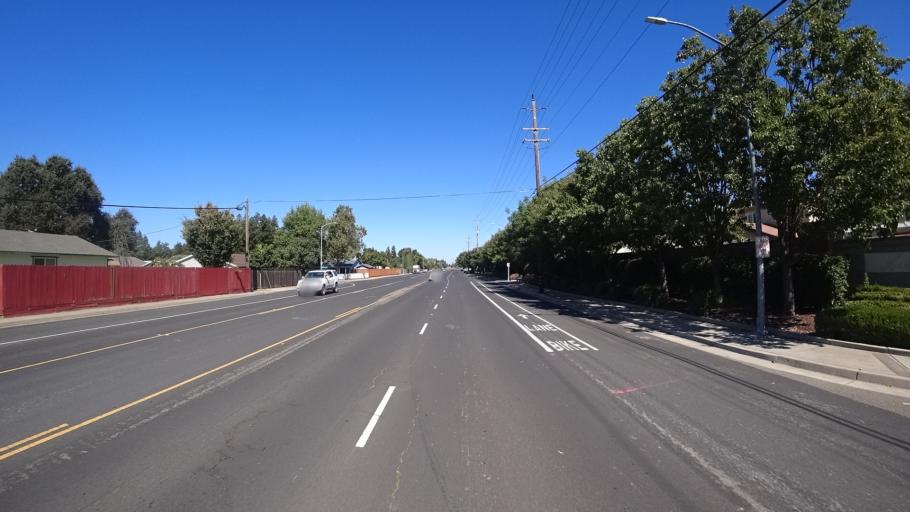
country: US
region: California
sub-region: Sacramento County
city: Elk Grove
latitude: 38.4055
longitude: -121.3529
